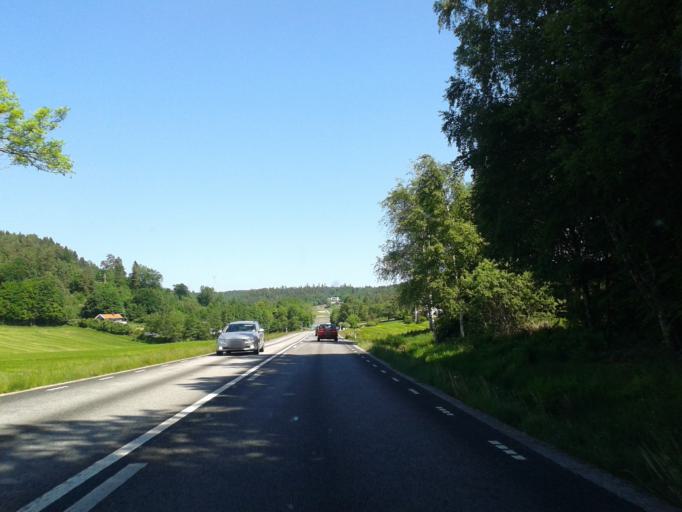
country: SE
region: Vaestra Goetaland
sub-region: Orust
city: Henan
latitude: 58.3332
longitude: 11.6879
